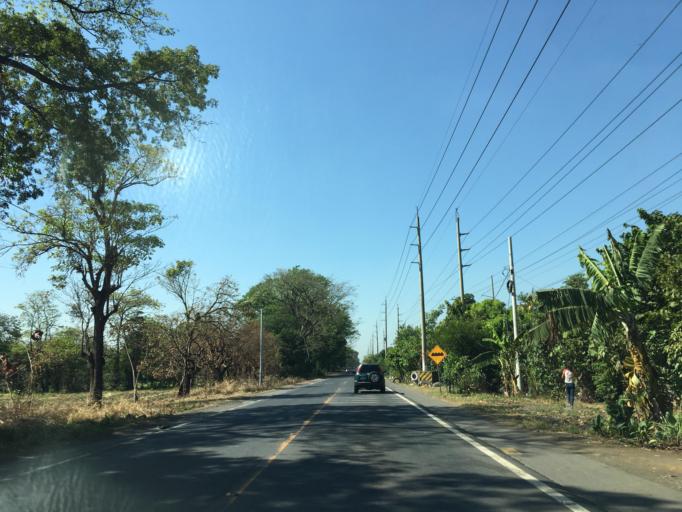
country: GT
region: Escuintla
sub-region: Municipio de Masagua
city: Masagua
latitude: 14.2193
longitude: -90.8326
